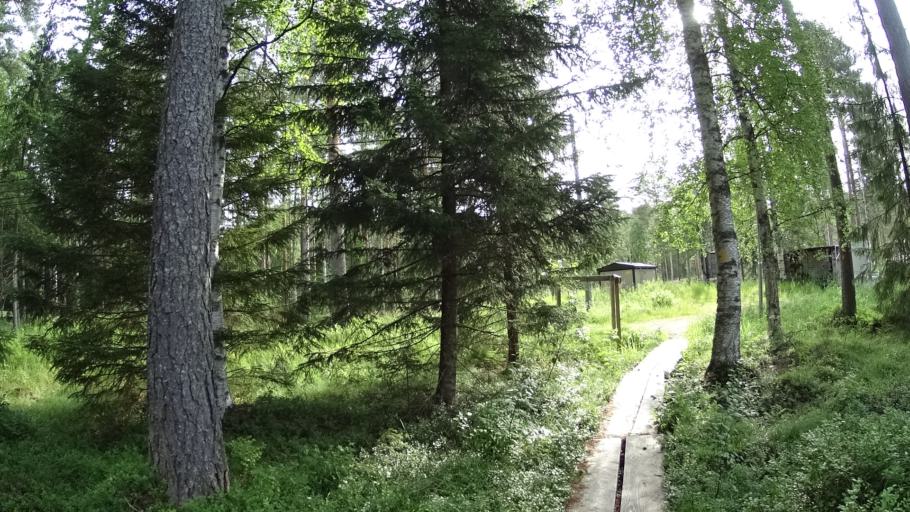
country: FI
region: Southern Ostrobothnia
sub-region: Kuusiokunnat
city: AEhtaeri
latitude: 62.5375
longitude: 24.1778
